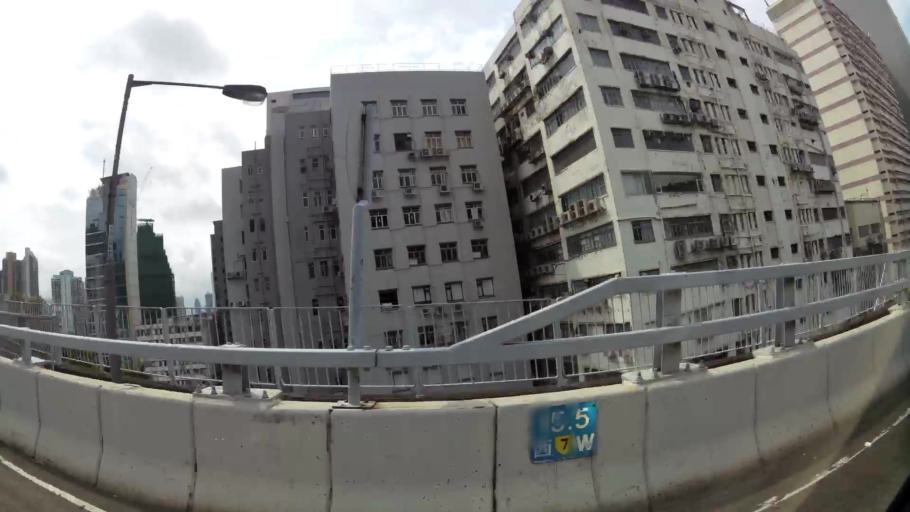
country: HK
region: Sham Shui Po
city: Sham Shui Po
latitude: 22.3408
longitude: 114.1502
